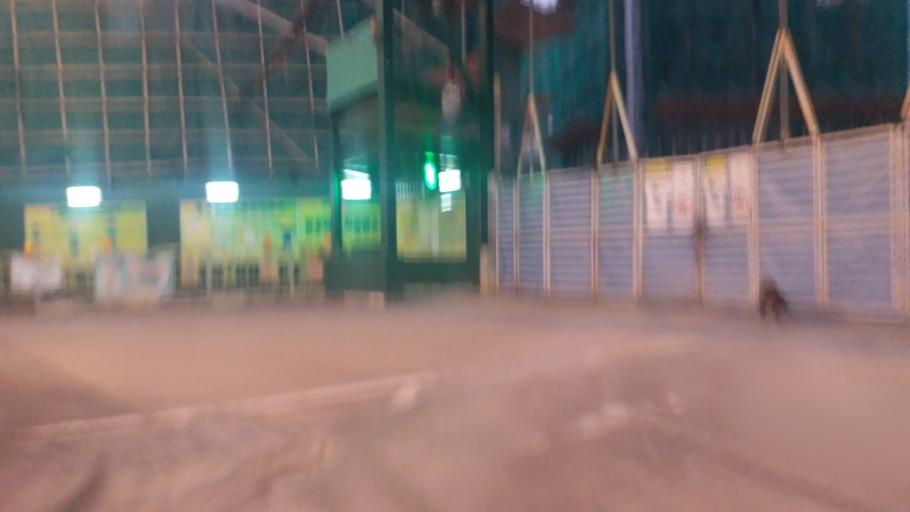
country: HK
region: Yuen Long
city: Yuen Long Kau Hui
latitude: 22.4667
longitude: 114.0057
